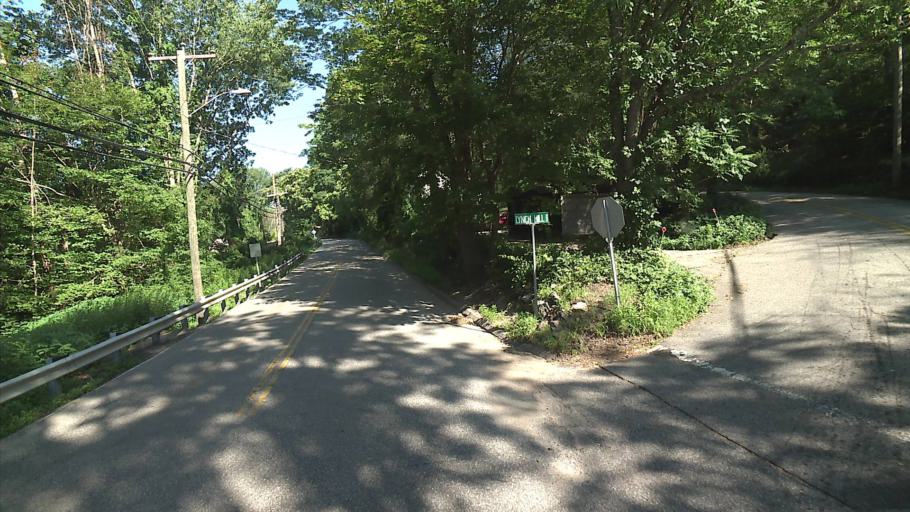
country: US
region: Connecticut
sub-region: New London County
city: Oxoboxo River
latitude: 41.4545
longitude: -72.1375
